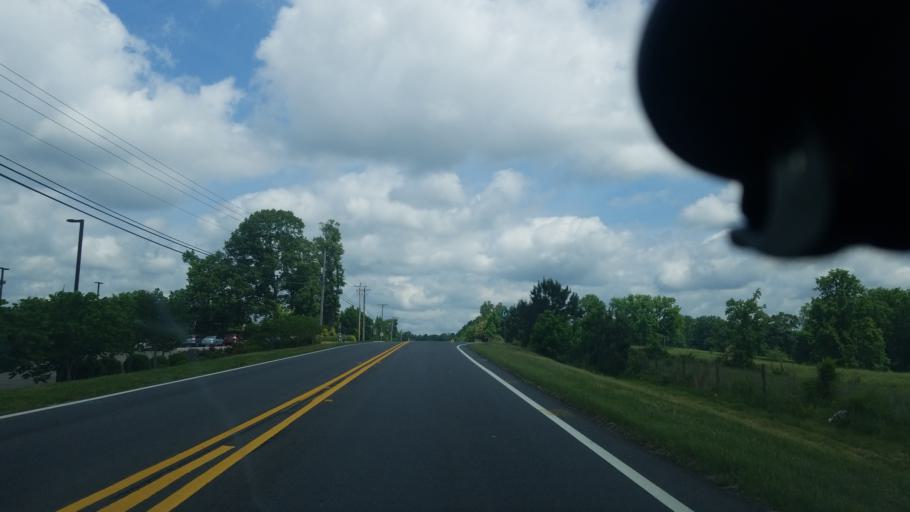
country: US
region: Georgia
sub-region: Forsyth County
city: Cumming
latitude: 34.2045
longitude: -84.2199
